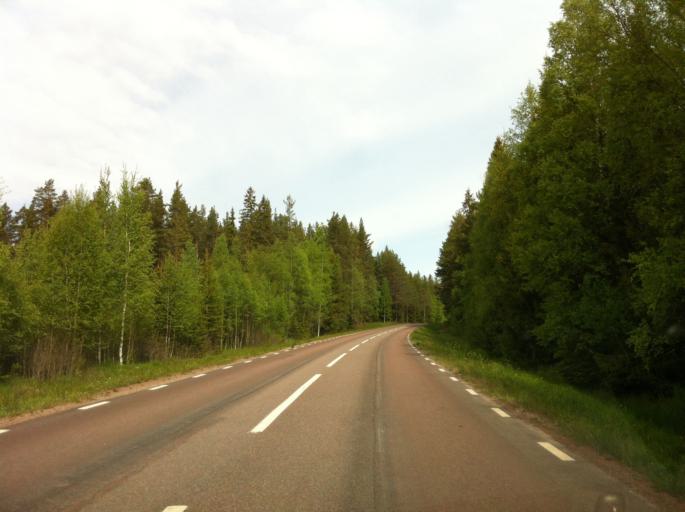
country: SE
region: Dalarna
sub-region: Leksand Municipality
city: Siljansnas
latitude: 60.7635
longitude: 14.7321
